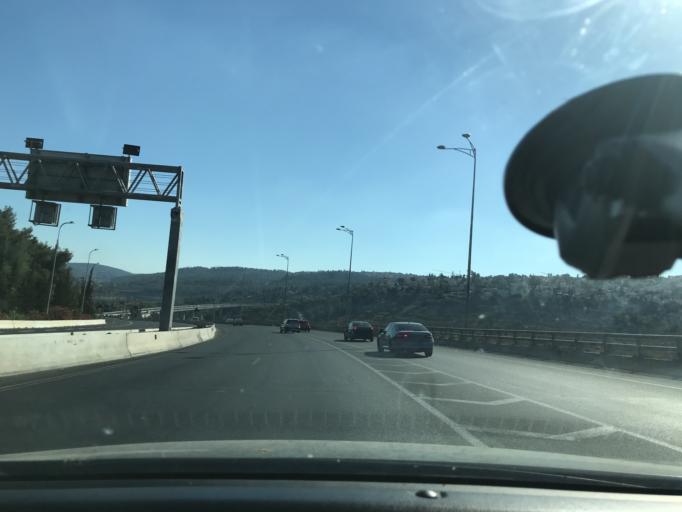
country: PS
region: West Bank
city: Bayt Iksa
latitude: 31.8011
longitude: 35.1750
